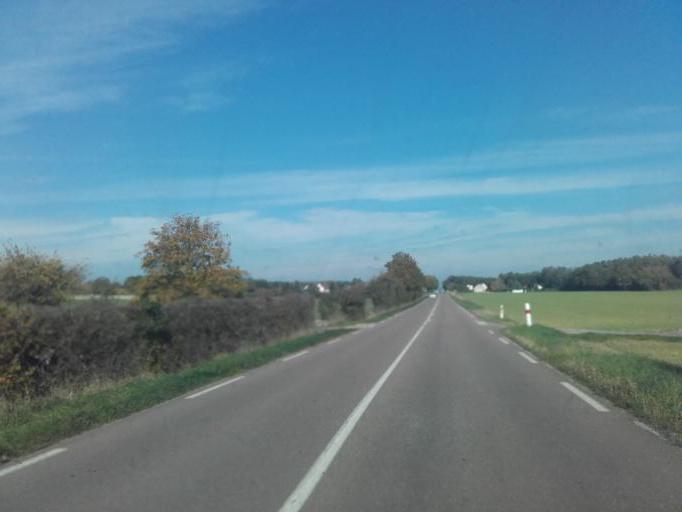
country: FR
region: Bourgogne
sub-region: Departement de Saone-et-Loire
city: Rully
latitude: 46.8908
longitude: 4.7523
